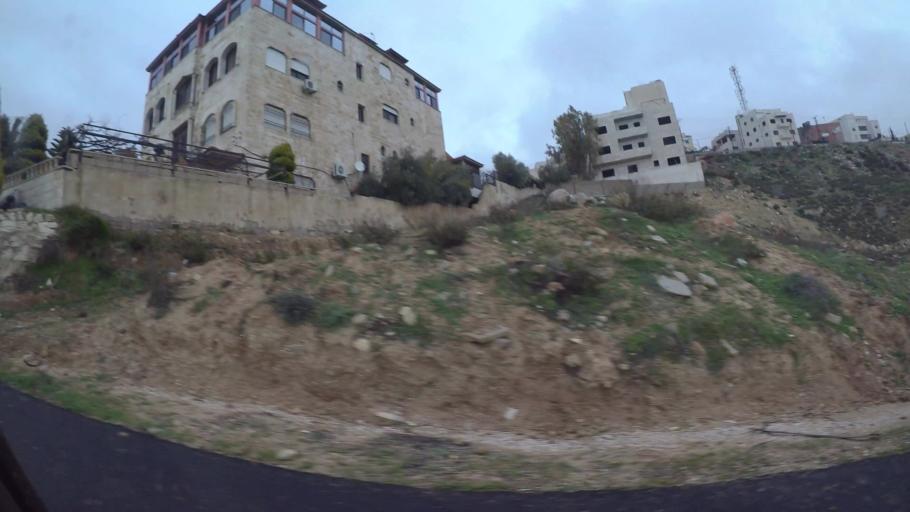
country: JO
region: Amman
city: Al Jubayhah
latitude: 32.0350
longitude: 35.8416
